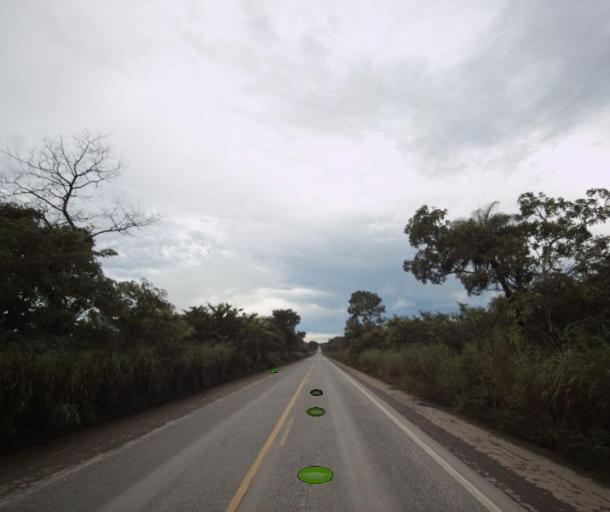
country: BR
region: Goias
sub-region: Porangatu
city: Porangatu
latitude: -13.5536
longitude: -49.0824
